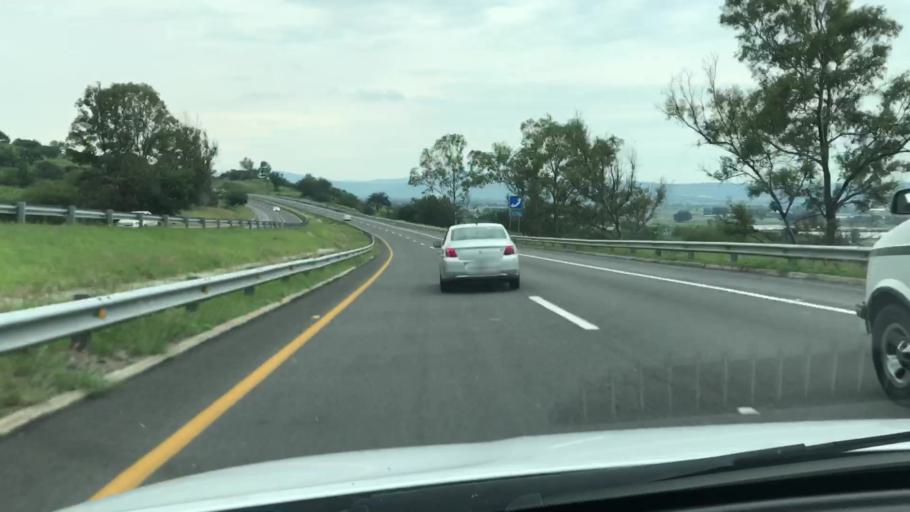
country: MX
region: Jalisco
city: Ocotlan
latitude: 20.4139
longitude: -102.7458
